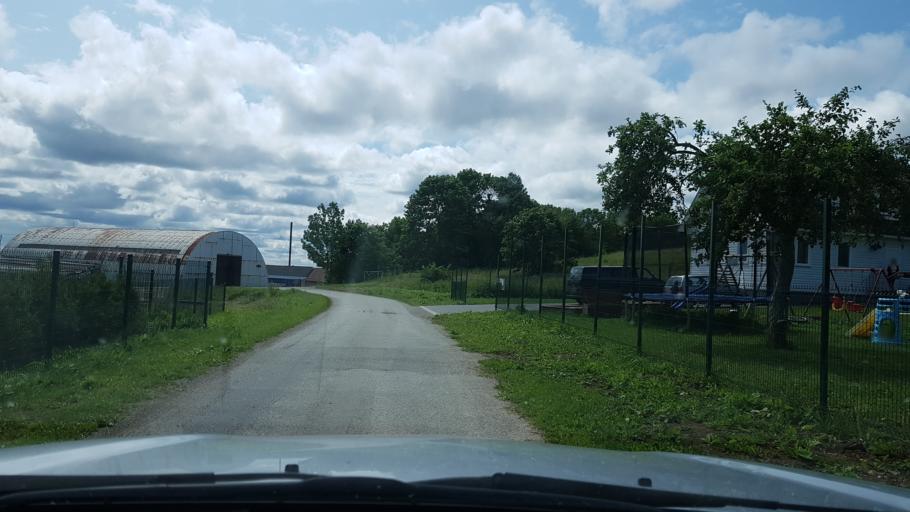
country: EE
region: Ida-Virumaa
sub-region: Sillamaee linn
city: Sillamae
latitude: 59.3746
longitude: 27.8685
